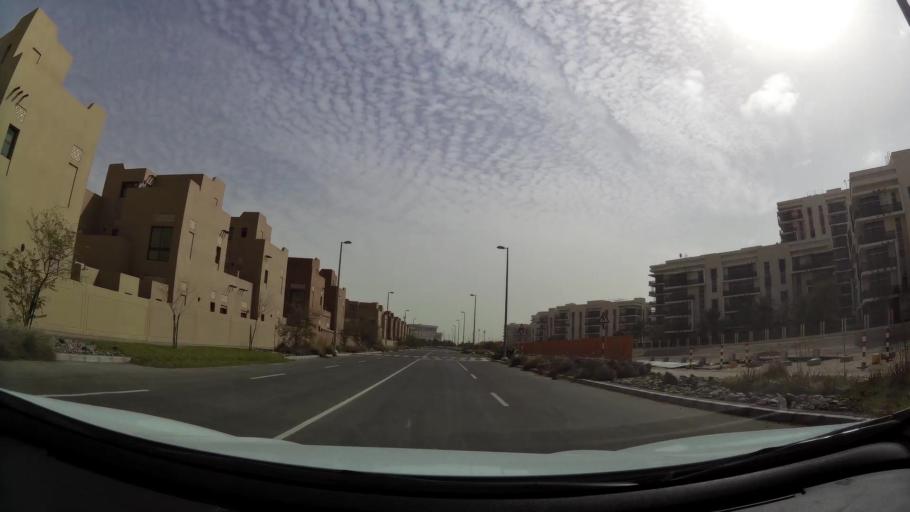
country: AE
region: Abu Dhabi
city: Abu Dhabi
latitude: 24.4149
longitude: 54.5368
